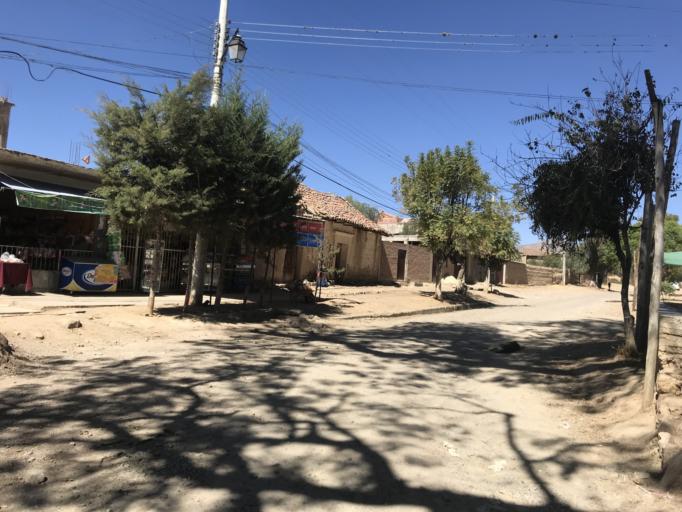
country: BO
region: Cochabamba
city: Tarata
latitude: -17.6143
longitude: -66.0255
